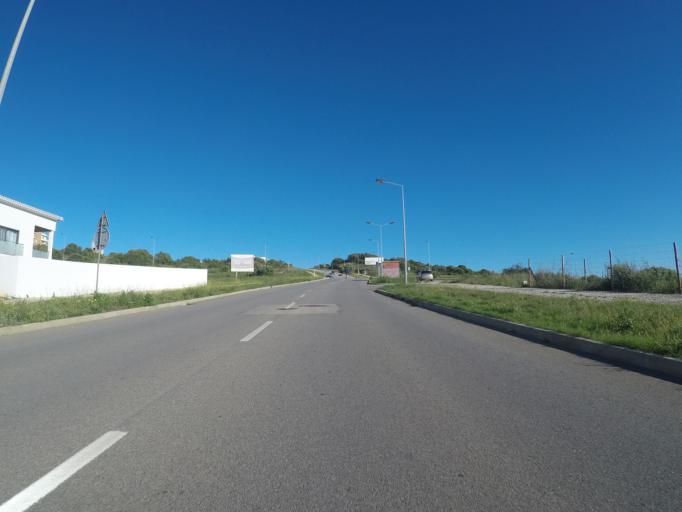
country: PT
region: Faro
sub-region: Lagos
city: Lagos
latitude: 37.0944
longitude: -8.6867
